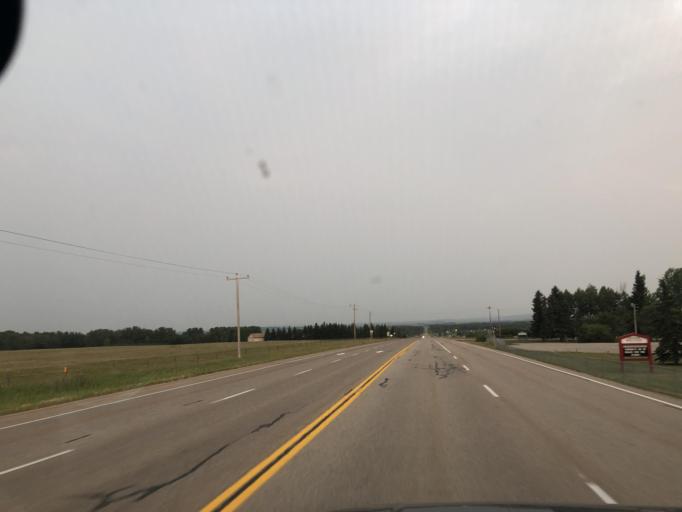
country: CA
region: Alberta
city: Cochrane
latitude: 51.0802
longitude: -114.3505
